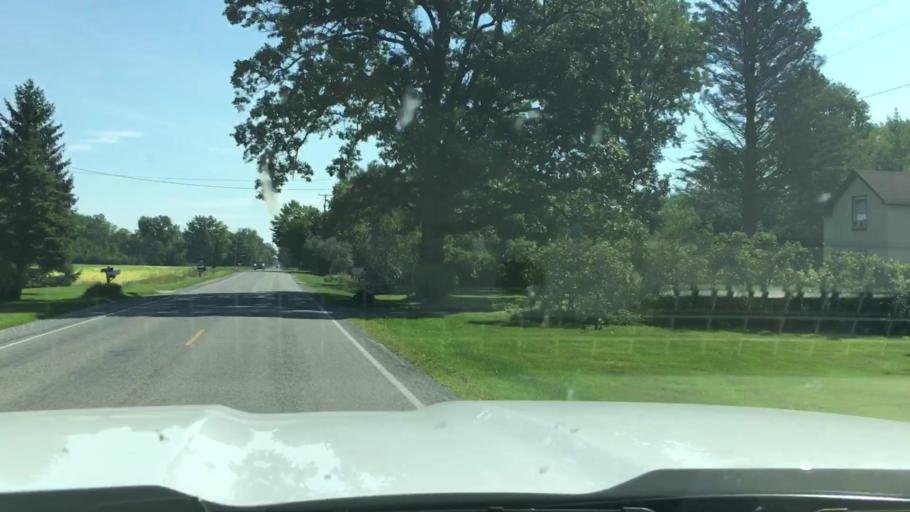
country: US
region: Michigan
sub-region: Saginaw County
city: Freeland
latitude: 43.5252
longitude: -84.1557
